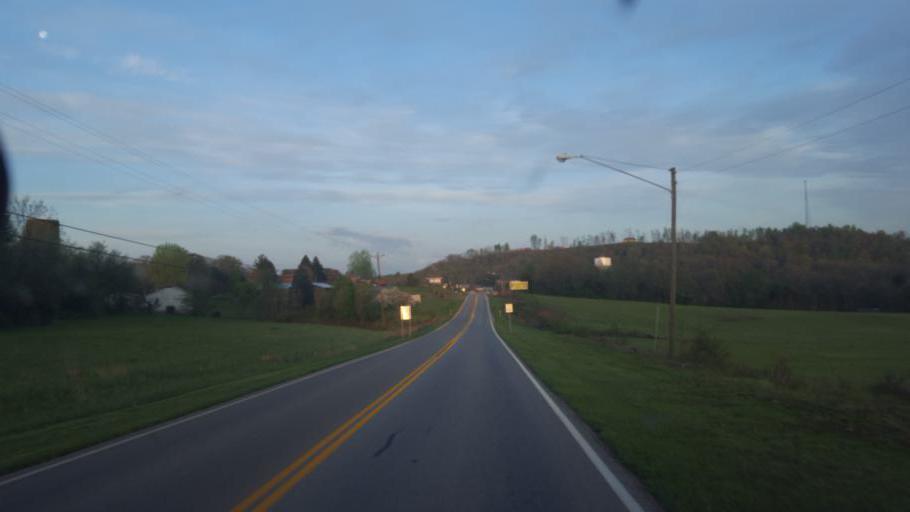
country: US
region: Kentucky
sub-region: Barren County
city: Cave City
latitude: 37.1356
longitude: -85.9874
